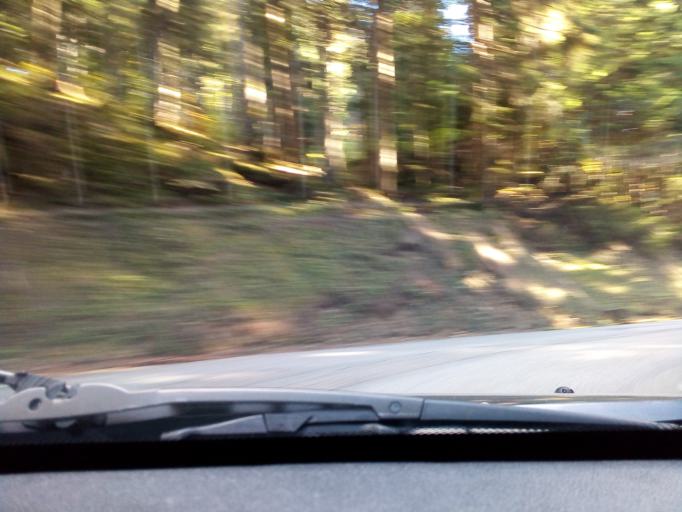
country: FR
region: Rhone-Alpes
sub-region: Departement de l'Isere
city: Le Sappey-en-Chartreuse
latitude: 45.2747
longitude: 5.7673
